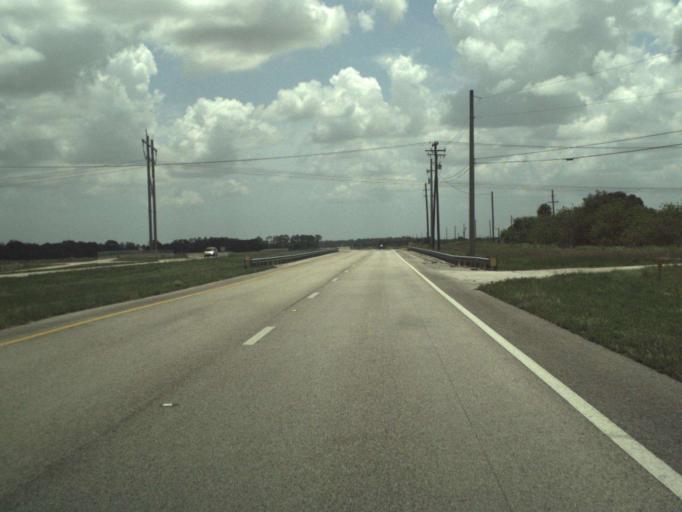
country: US
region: Florida
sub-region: Saint Lucie County
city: Fort Pierce South
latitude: 27.3679
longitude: -80.5487
